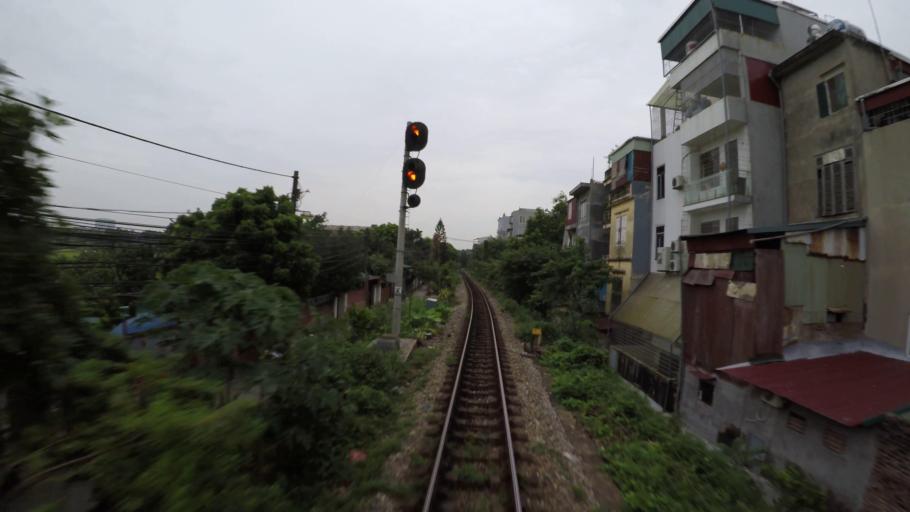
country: VN
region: Ha Noi
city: Trau Quy
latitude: 21.0395
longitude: 105.8978
